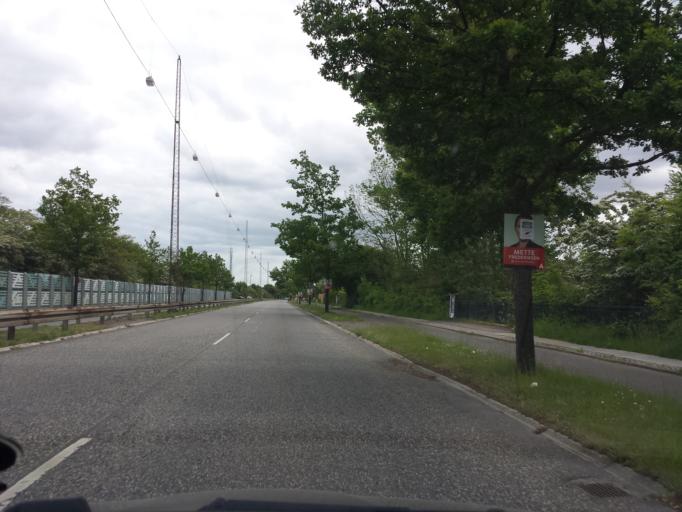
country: DK
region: Capital Region
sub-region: Herlev Kommune
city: Herlev
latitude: 55.7180
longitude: 12.4083
